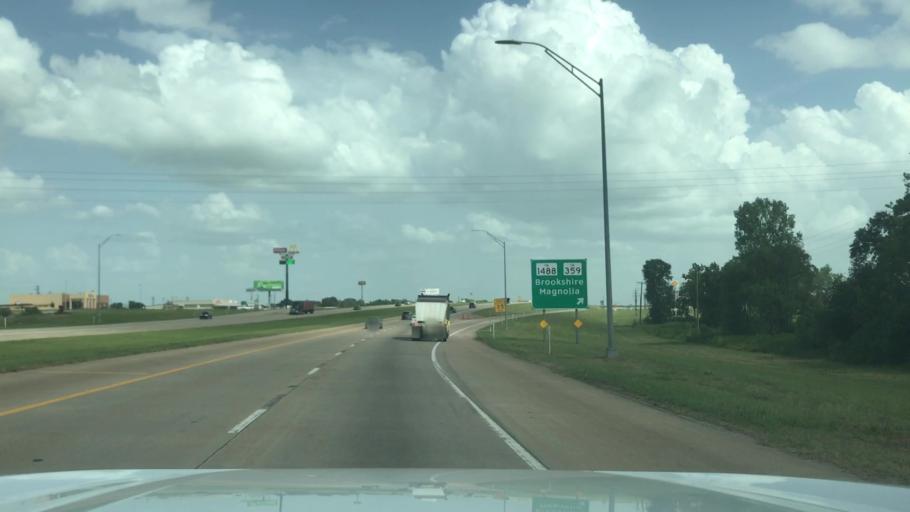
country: US
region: Texas
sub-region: Waller County
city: Hempstead
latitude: 30.1105
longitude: -96.0529
